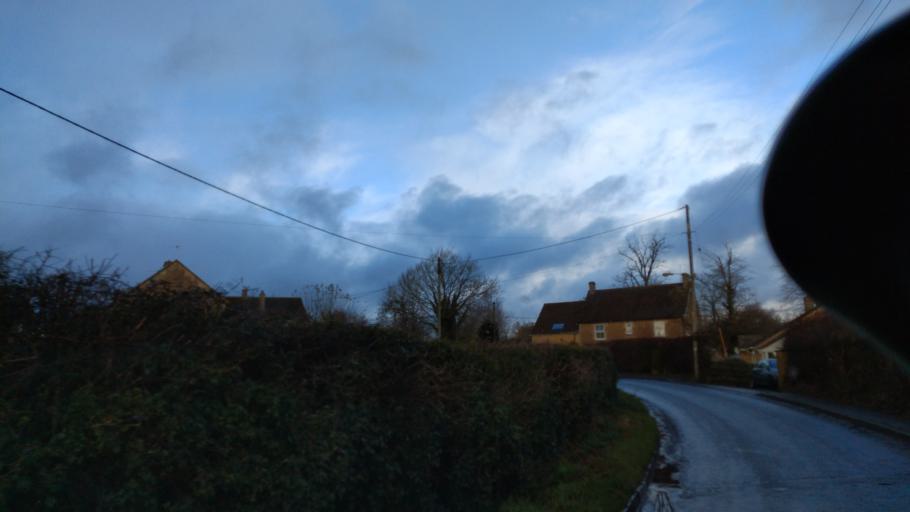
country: GB
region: England
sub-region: Wiltshire
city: Atworth
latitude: 51.3954
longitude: -2.1695
